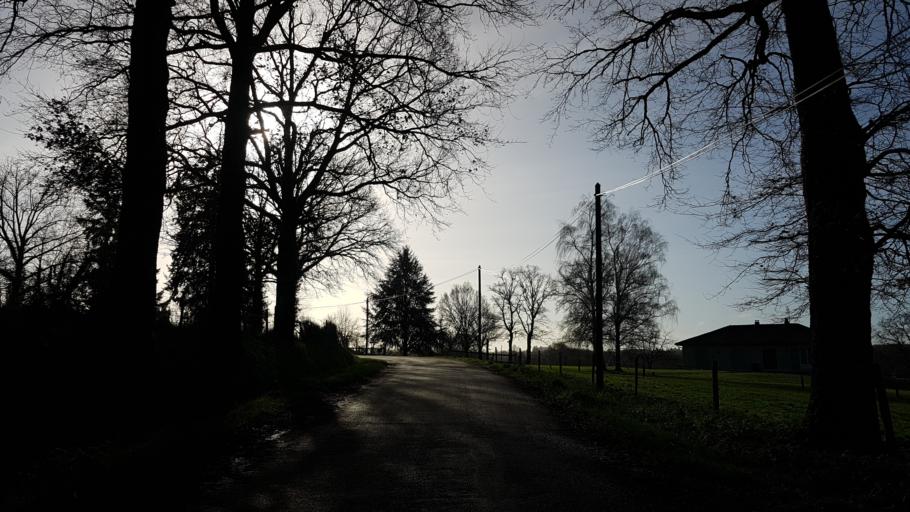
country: FR
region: Poitou-Charentes
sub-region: Departement de la Charente
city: Etagnac
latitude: 45.9297
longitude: 0.8045
